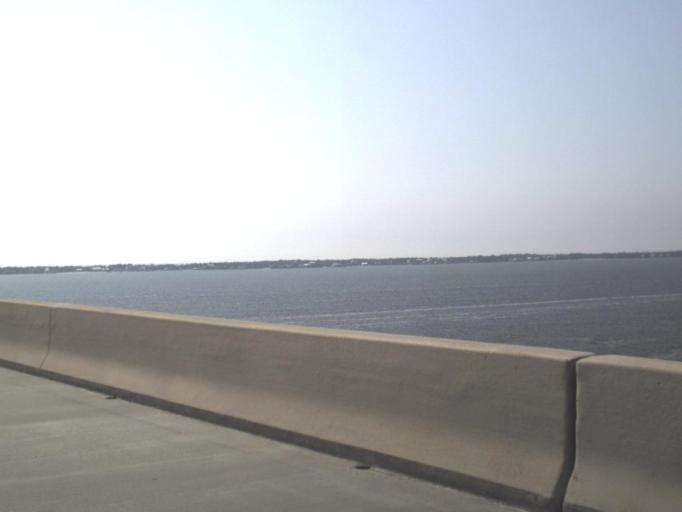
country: US
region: Florida
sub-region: Franklin County
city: Eastpoint
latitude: 29.6847
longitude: -84.8813
